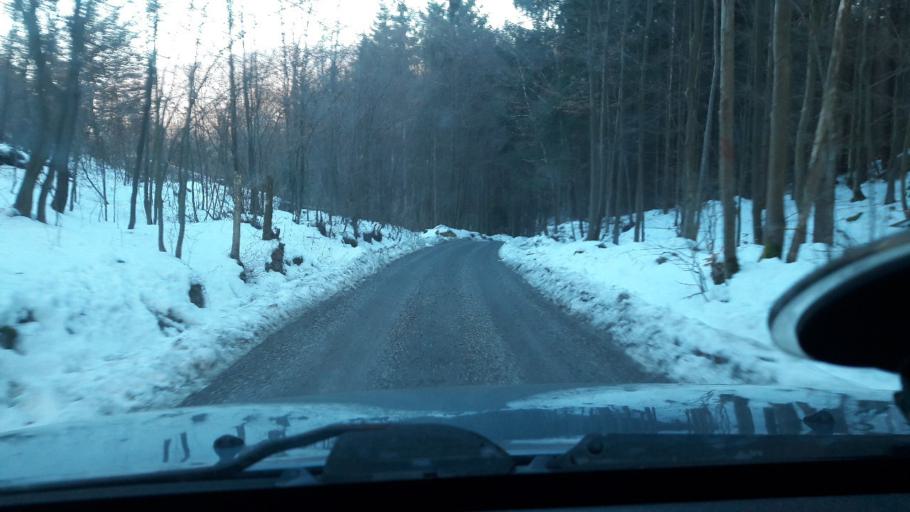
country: SK
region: Banskobystricky
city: Zarnovica
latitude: 48.5066
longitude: 18.7168
